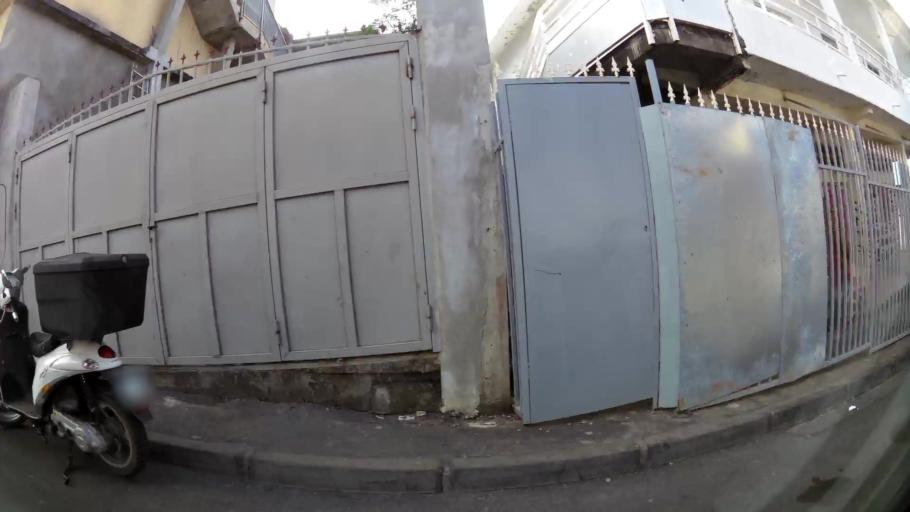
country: YT
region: Mamoudzou
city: Mamoudzou
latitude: -12.7804
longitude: 45.2296
